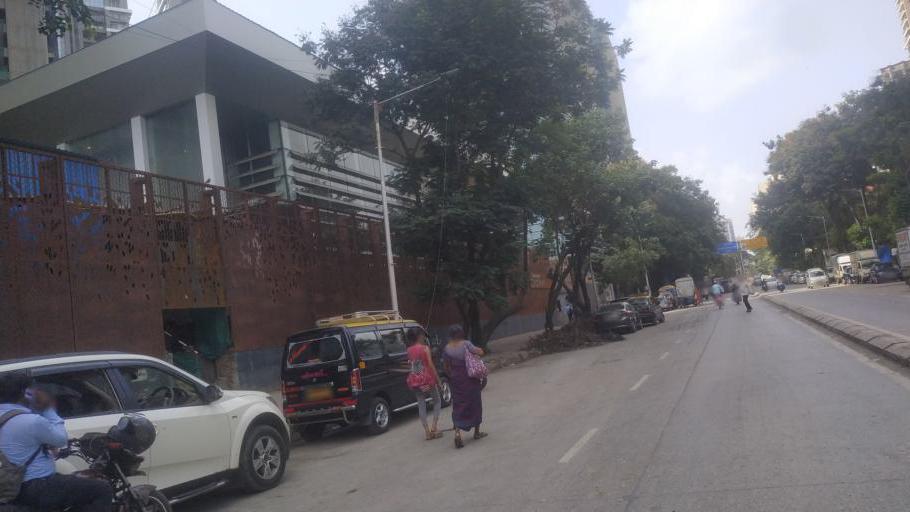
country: IN
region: Maharashtra
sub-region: Mumbai Suburban
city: Mumbai
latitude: 19.0096
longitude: 72.8308
